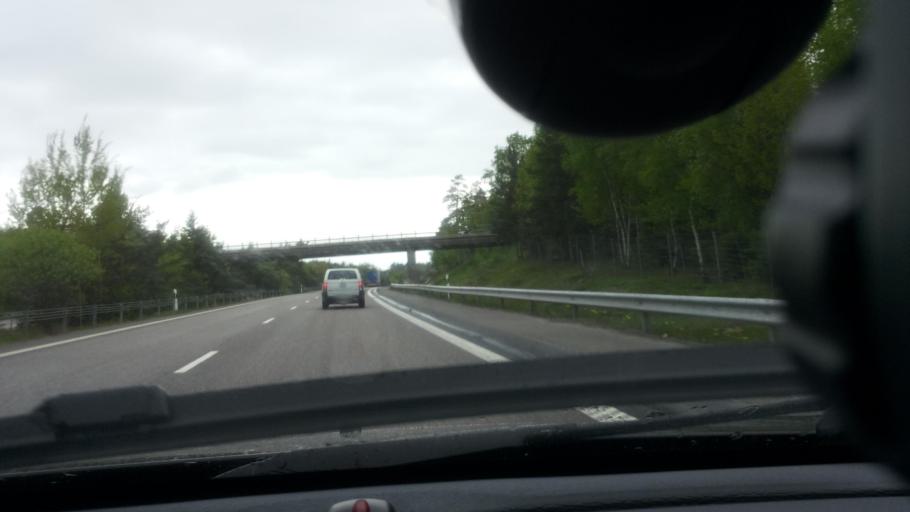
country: SE
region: Uppsala
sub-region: Knivsta Kommun
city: Knivsta
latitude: 59.7208
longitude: 17.8423
